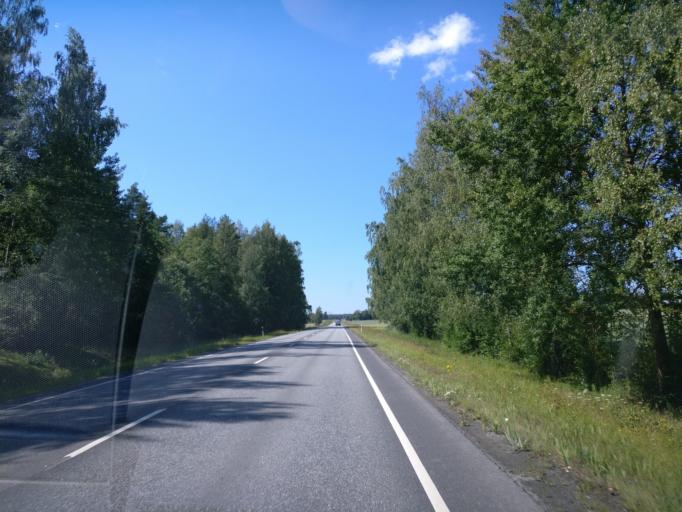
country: FI
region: Satakunta
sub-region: Pori
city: Nakkila
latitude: 61.4587
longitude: 22.0247
